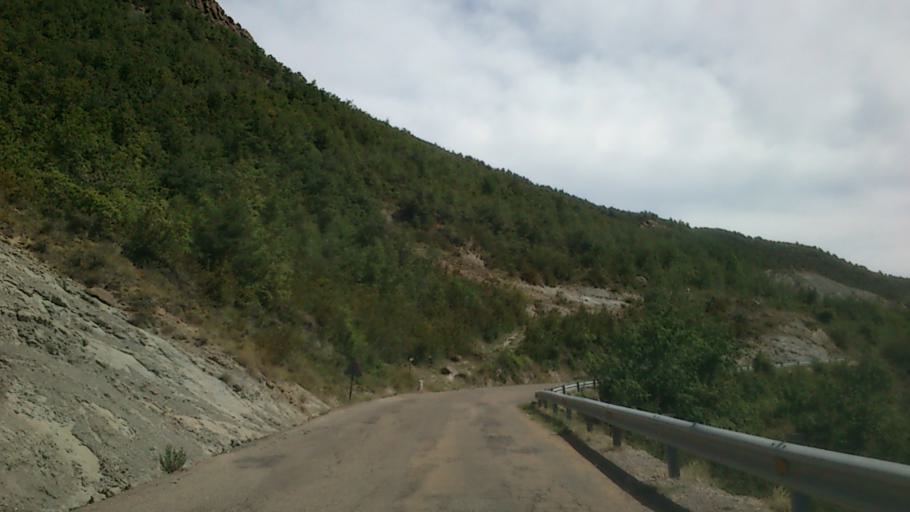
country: ES
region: Aragon
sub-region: Provincia de Huesca
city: Arguis
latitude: 42.3189
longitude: -0.4389
